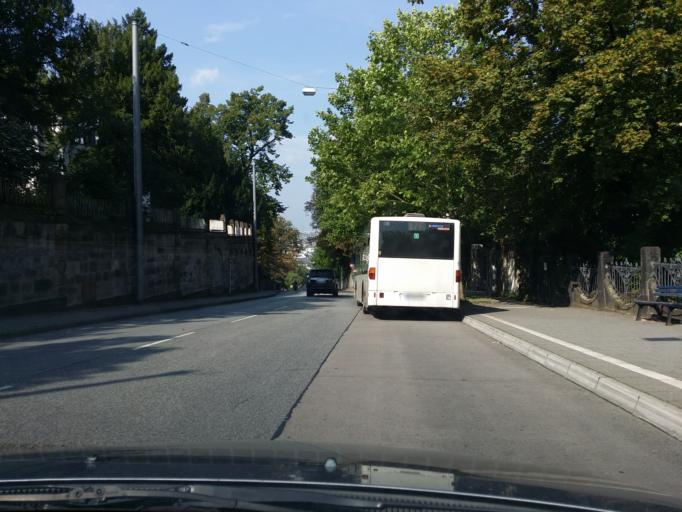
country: DE
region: Hesse
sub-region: Regierungsbezirk Darmstadt
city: Wiesbaden
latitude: 50.0822
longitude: 8.2550
